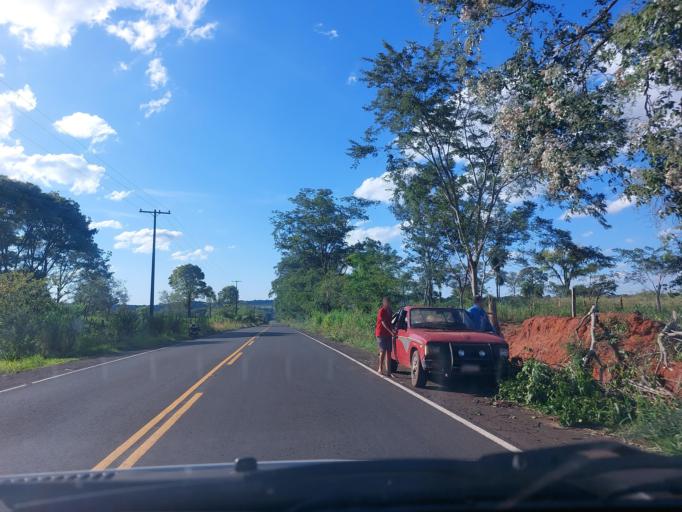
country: PY
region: San Pedro
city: Guayaybi
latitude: -24.5593
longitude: -56.5197
